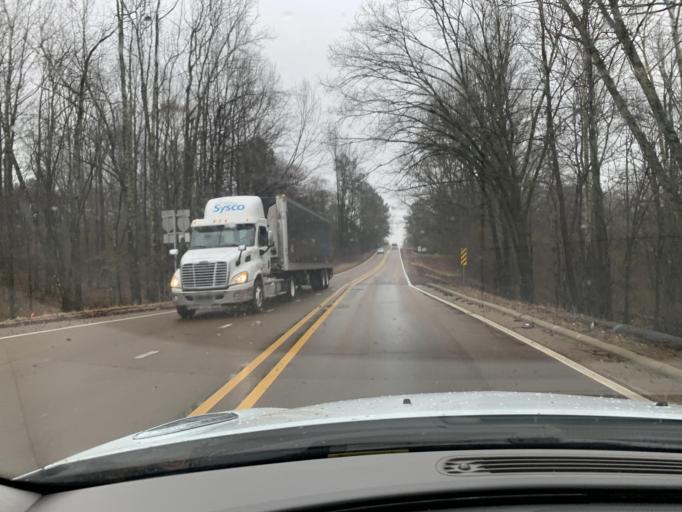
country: US
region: Mississippi
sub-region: De Soto County
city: Hernando
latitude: 34.8828
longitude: -89.9961
